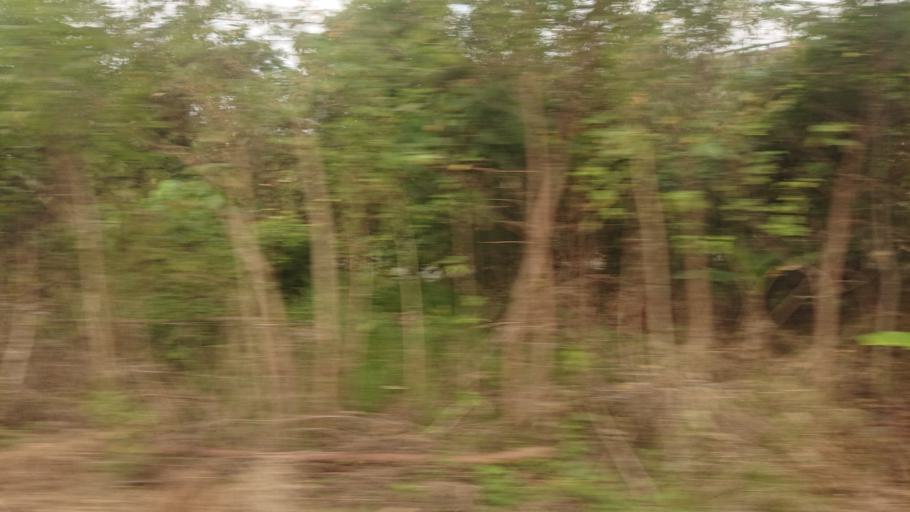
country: TW
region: Taiwan
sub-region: Yunlin
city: Douliu
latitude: 23.7735
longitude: 120.6369
